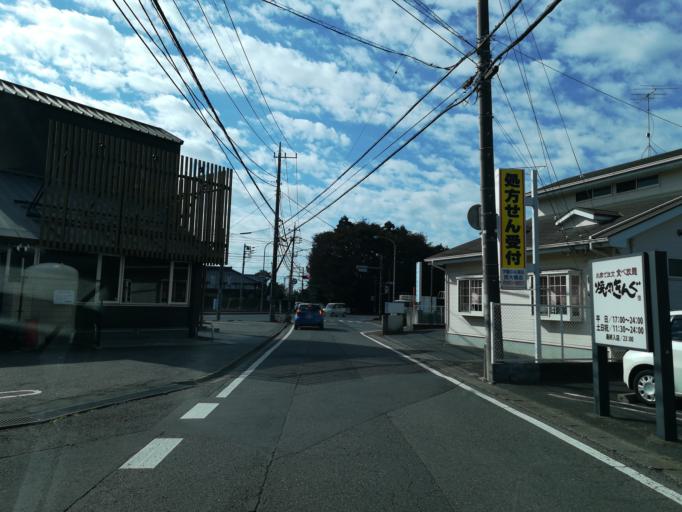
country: JP
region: Ibaraki
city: Naka
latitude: 36.0720
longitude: 140.0918
